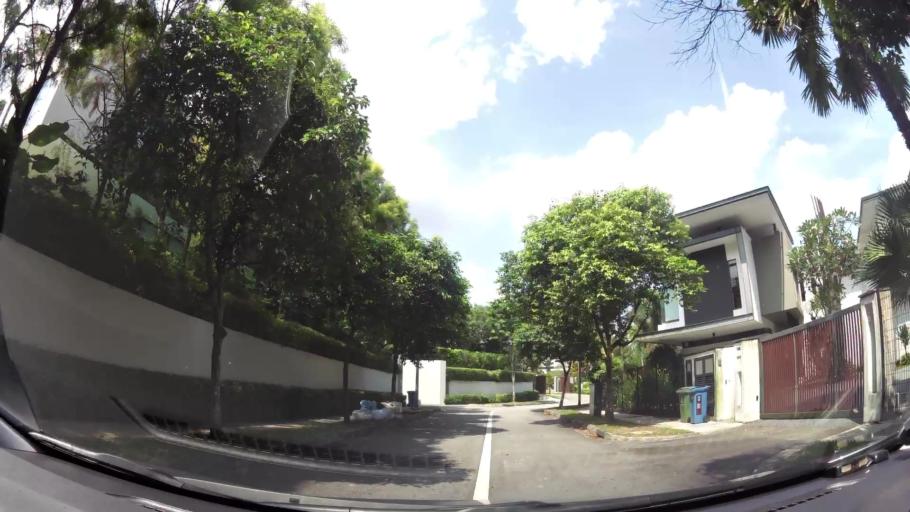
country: SG
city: Singapore
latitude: 1.3081
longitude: 103.8054
